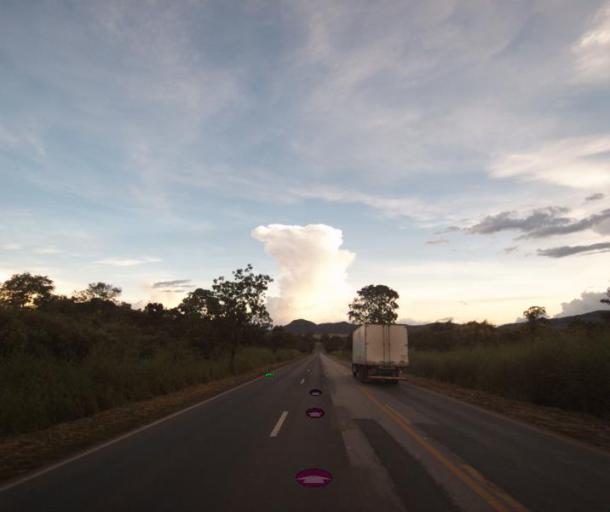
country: BR
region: Goias
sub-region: Uruacu
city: Uruacu
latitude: -14.3452
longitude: -49.1570
